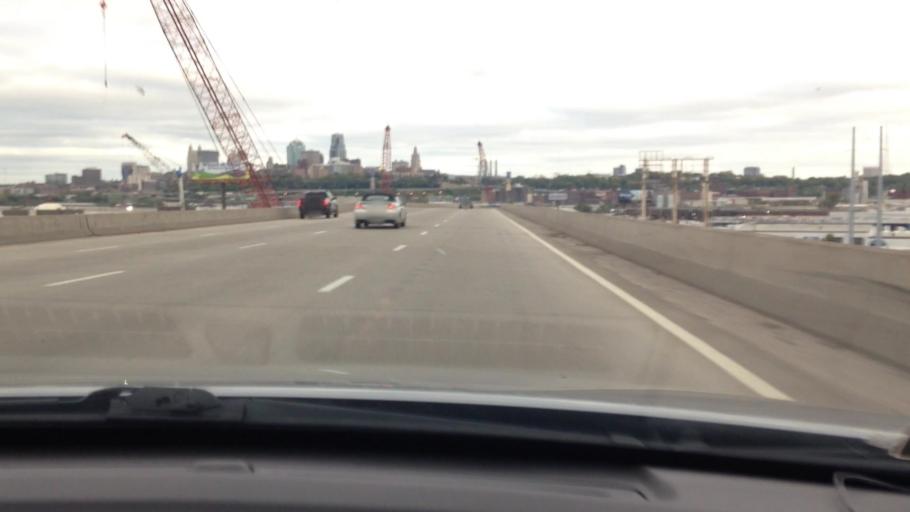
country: US
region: Kansas
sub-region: Wyandotte County
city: Kansas City
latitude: 39.1132
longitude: -94.6154
